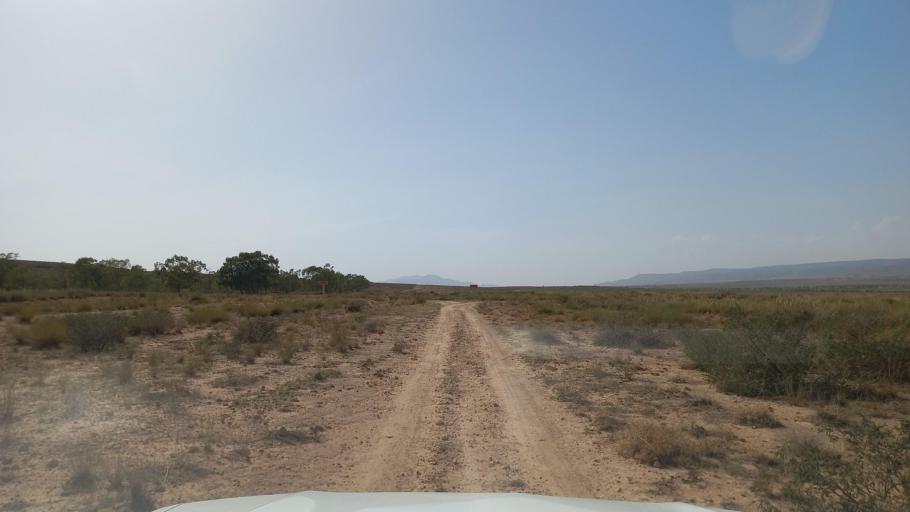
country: TN
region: Al Qasrayn
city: Kasserine
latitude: 35.2142
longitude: 8.9973
